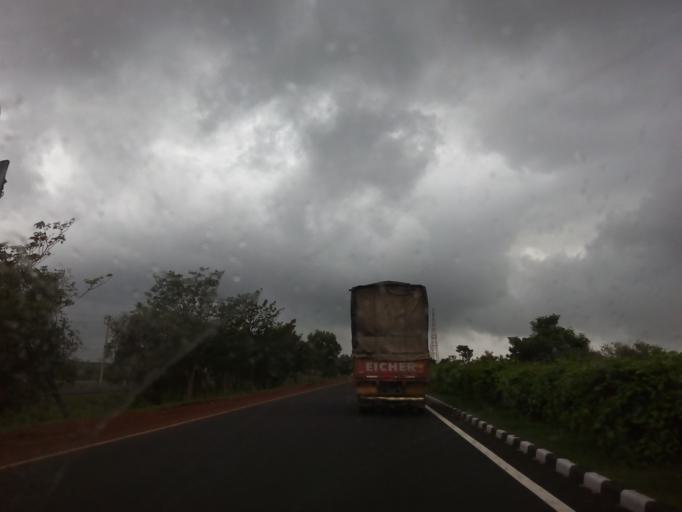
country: IN
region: Karnataka
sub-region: Belgaum
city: Belgaum
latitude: 16.0226
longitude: 74.5219
